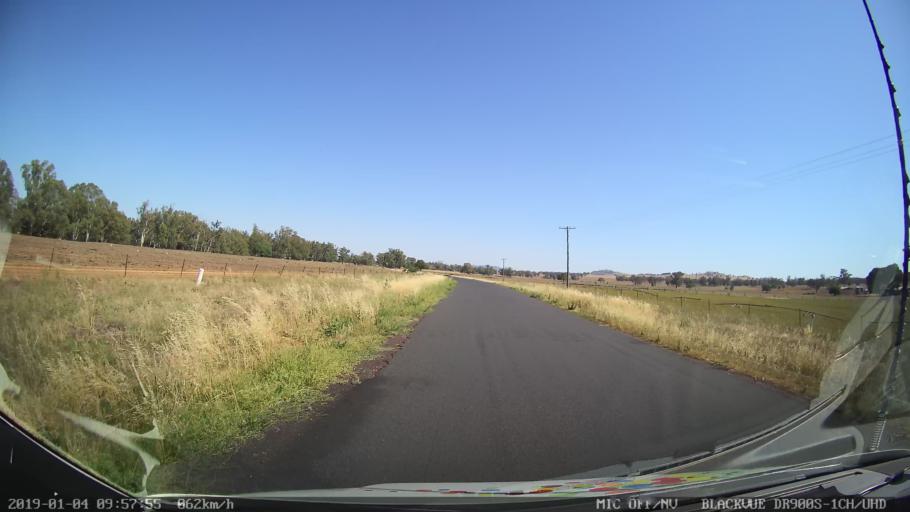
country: AU
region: New South Wales
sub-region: Cabonne
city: Canowindra
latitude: -33.5234
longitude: 148.3980
